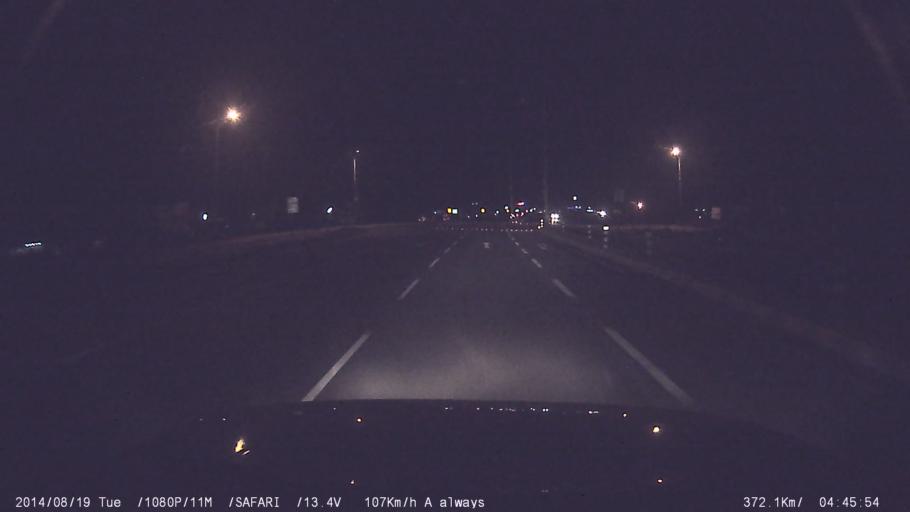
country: IN
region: Tamil Nadu
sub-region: Erode
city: Bhavani
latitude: 11.4433
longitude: 77.7142
